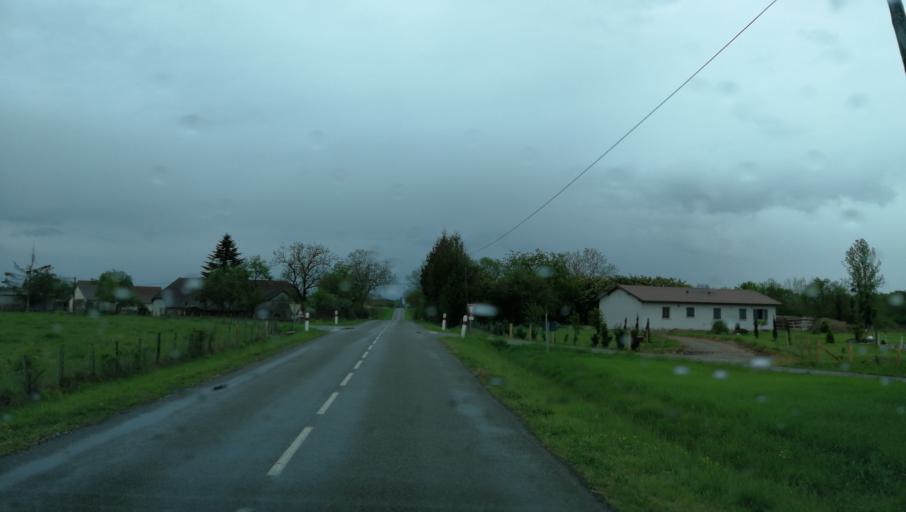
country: FR
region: Franche-Comte
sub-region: Departement du Jura
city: Bletterans
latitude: 46.8148
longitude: 5.3902
